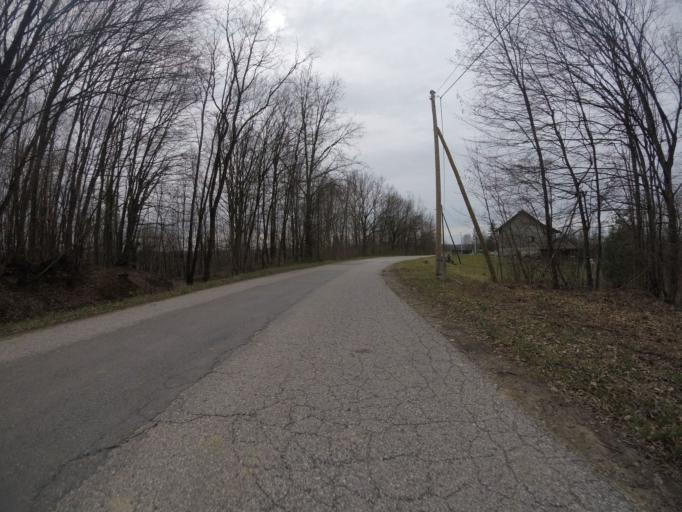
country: HR
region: Zagrebacka
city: Lukavec
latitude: 45.5818
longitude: 15.9646
